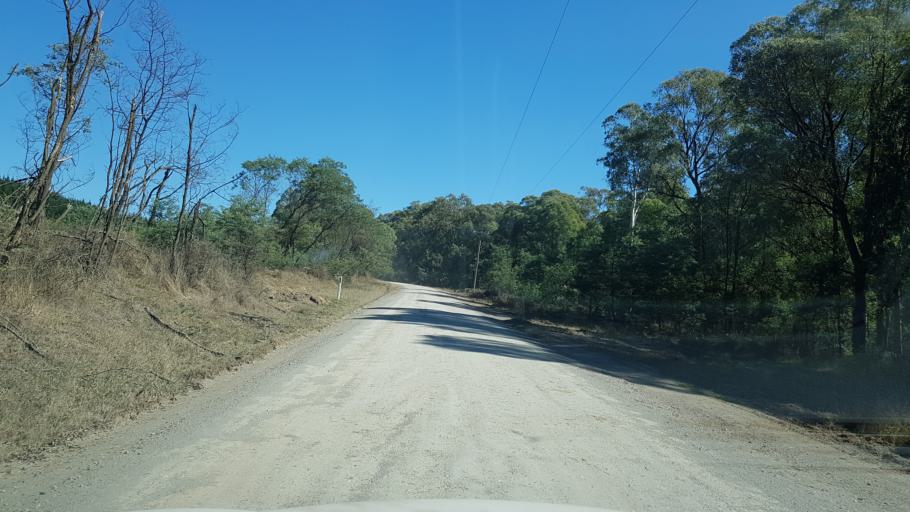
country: AU
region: Victoria
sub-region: Mansfield
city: Mansfield
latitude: -36.8526
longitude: 146.5215
